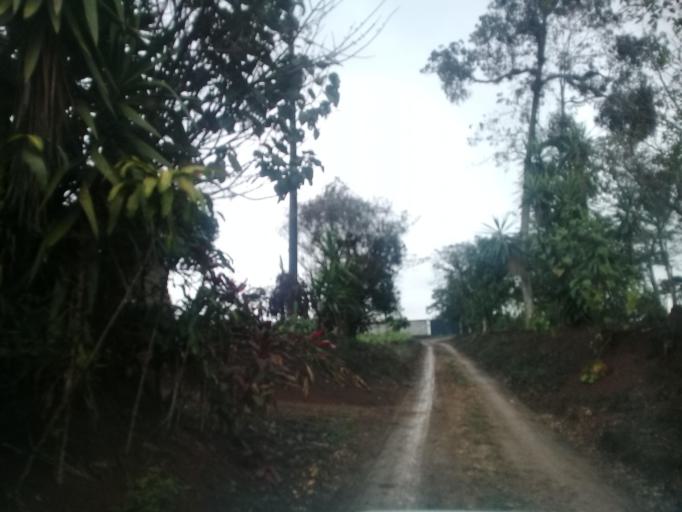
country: MX
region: Veracruz
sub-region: Amatlan de los Reyes
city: Centro de Readaptacion Social
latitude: 18.8185
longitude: -96.9413
